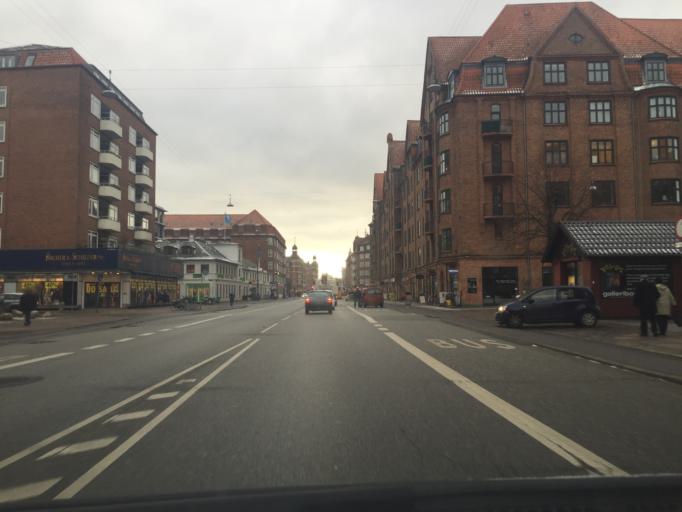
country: DK
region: Capital Region
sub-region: Kobenhavn
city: Christianshavn
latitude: 55.6671
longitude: 12.5978
